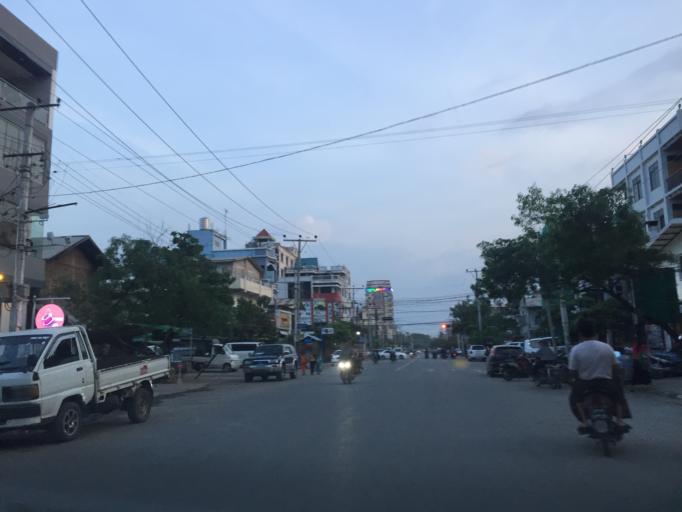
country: MM
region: Mandalay
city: Mandalay
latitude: 21.9700
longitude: 96.0881
